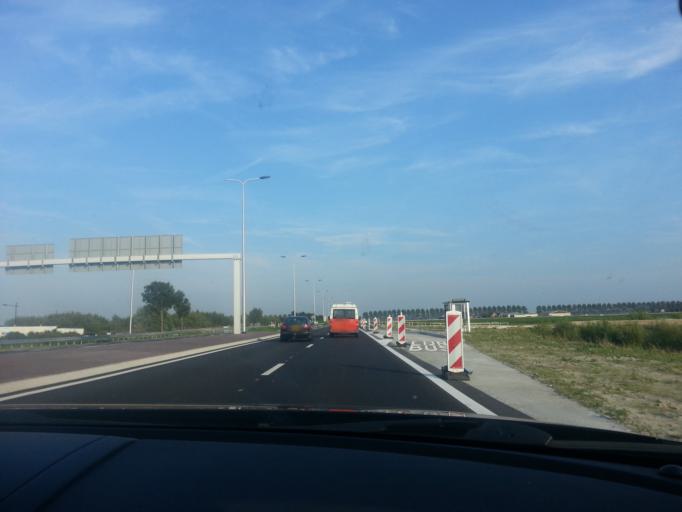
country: NL
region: South Holland
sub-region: Gemeente Hillegom
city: Hillegom
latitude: 52.2594
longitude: 4.6038
